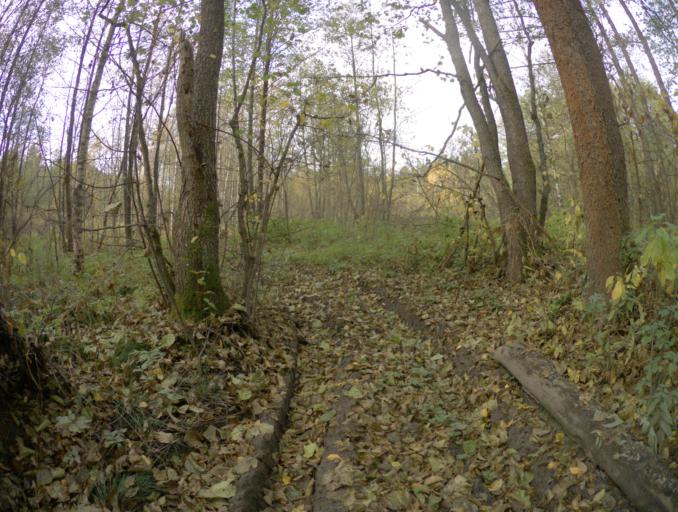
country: RU
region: Vladimir
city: Raduzhnyy
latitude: 55.9498
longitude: 40.3368
